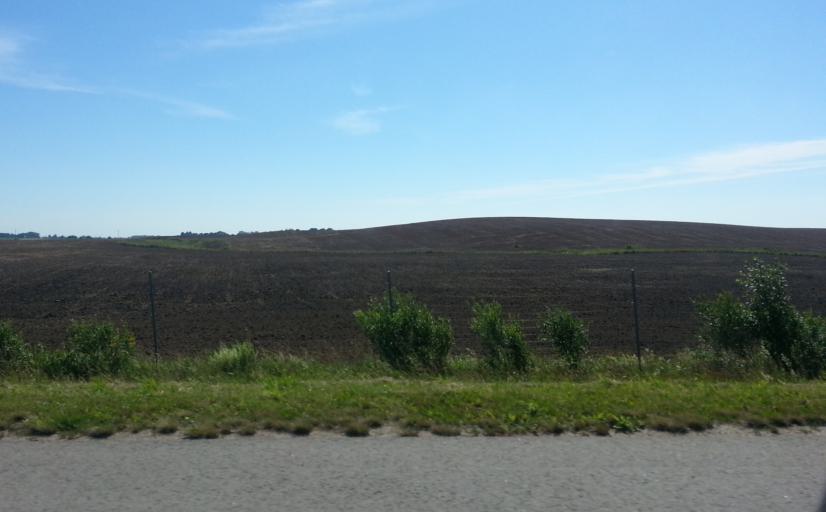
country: LT
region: Vilnius County
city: Ukmerge
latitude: 55.1972
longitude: 24.8140
